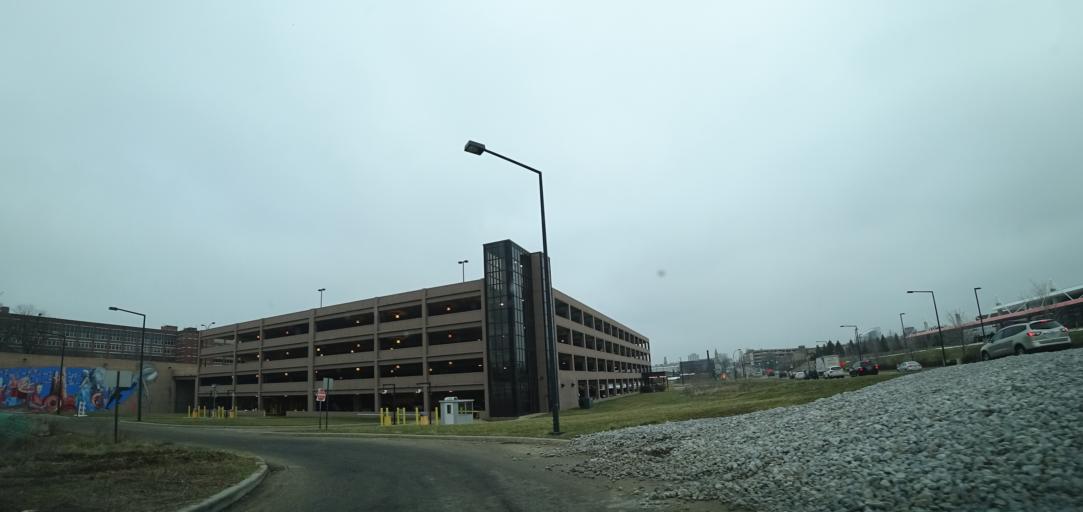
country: US
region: Ohio
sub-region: Summit County
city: Akron
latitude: 41.0698
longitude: -81.5241
